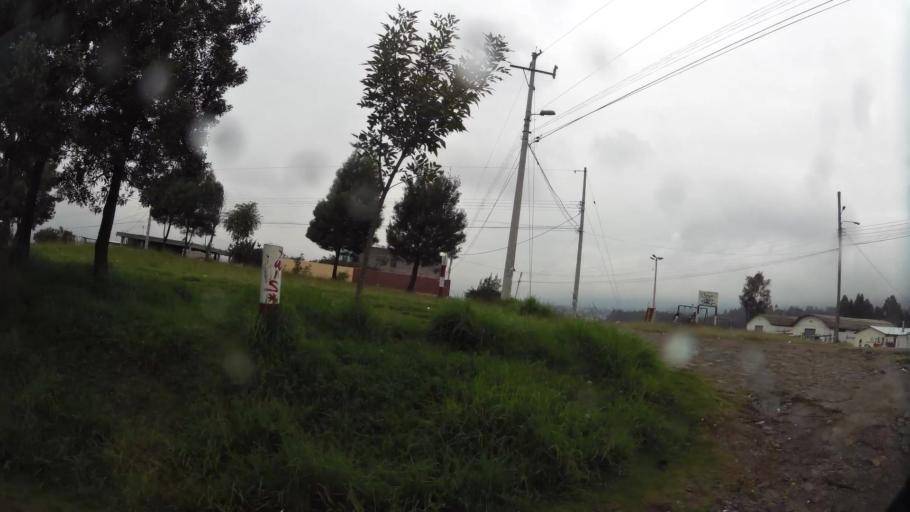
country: EC
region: Pichincha
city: Sangolqui
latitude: -0.2782
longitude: -78.4753
